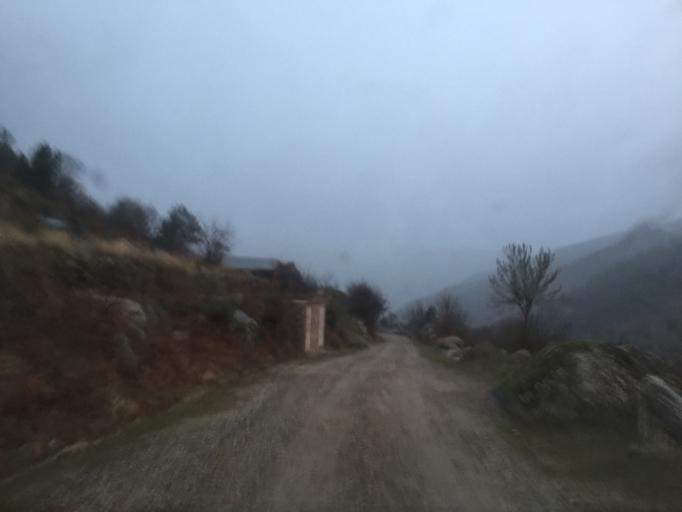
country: PT
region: Guarda
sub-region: Manteigas
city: Manteigas
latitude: 40.3784
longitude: -7.5498
